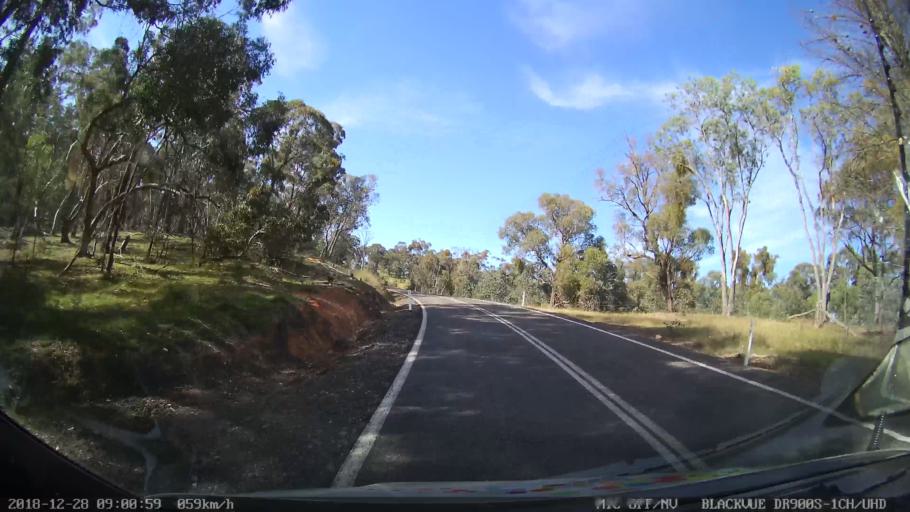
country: AU
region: New South Wales
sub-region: Upper Lachlan Shire
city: Crookwell
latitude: -34.1431
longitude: 149.3337
